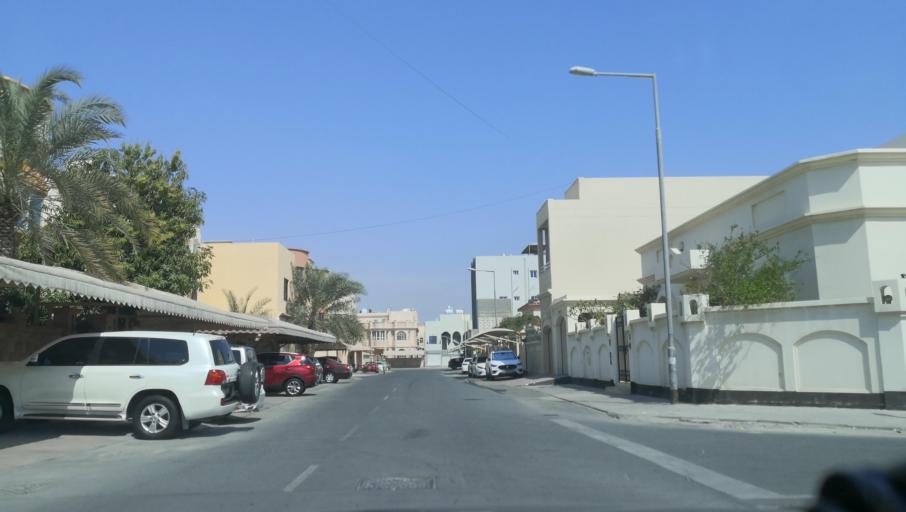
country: BH
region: Muharraq
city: Al Hadd
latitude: 26.2523
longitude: 50.6478
